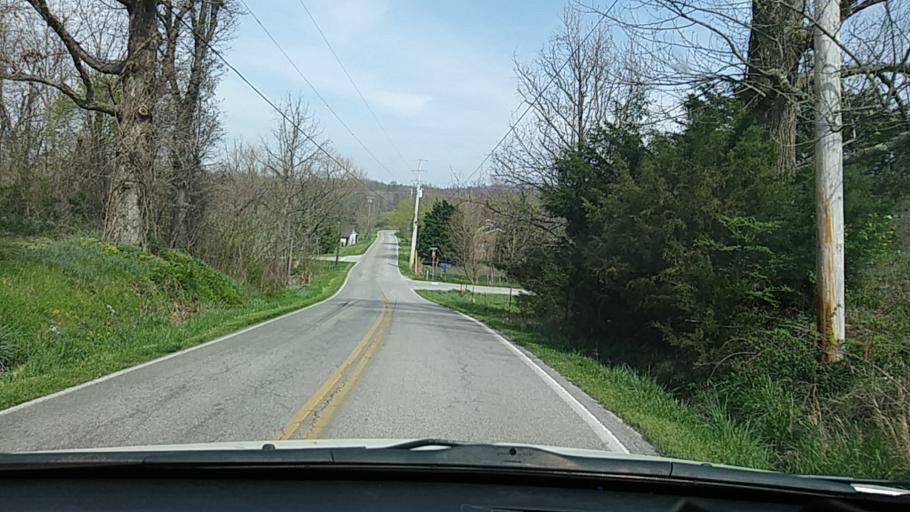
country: US
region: Tennessee
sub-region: Greene County
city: Tusculum
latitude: 36.0952
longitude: -82.7133
